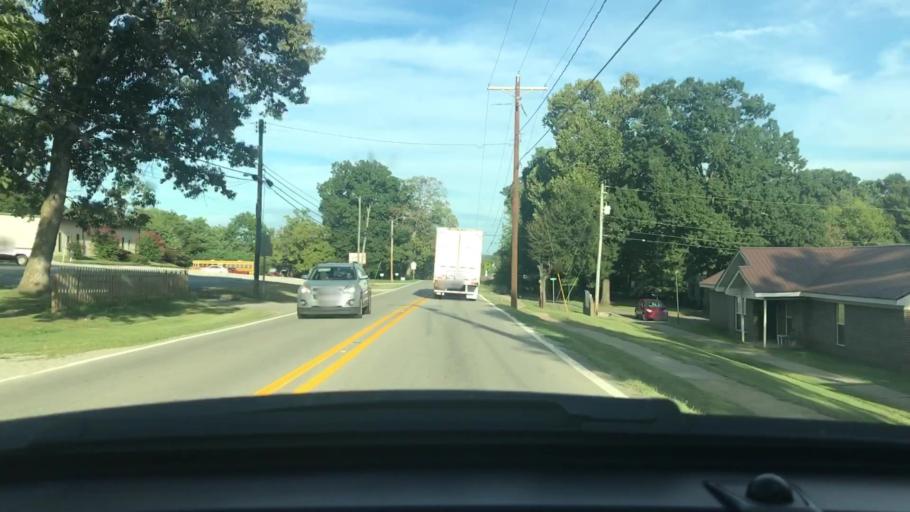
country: US
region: Arkansas
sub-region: Randolph County
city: Pocahontas
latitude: 36.2038
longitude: -91.1815
